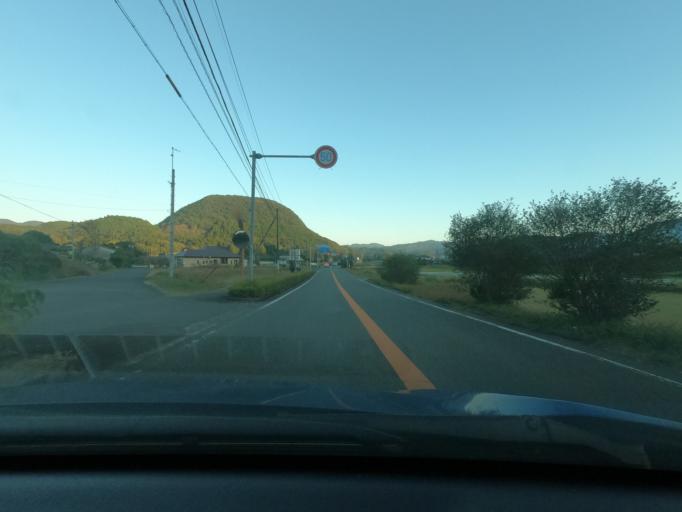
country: JP
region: Kagoshima
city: Satsumasendai
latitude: 31.8046
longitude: 130.3958
